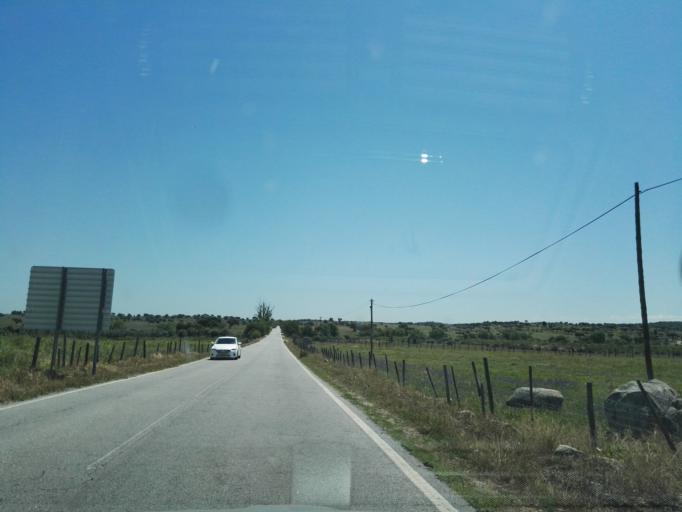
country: PT
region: Portalegre
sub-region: Arronches
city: Arronches
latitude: 39.0102
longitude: -7.2424
